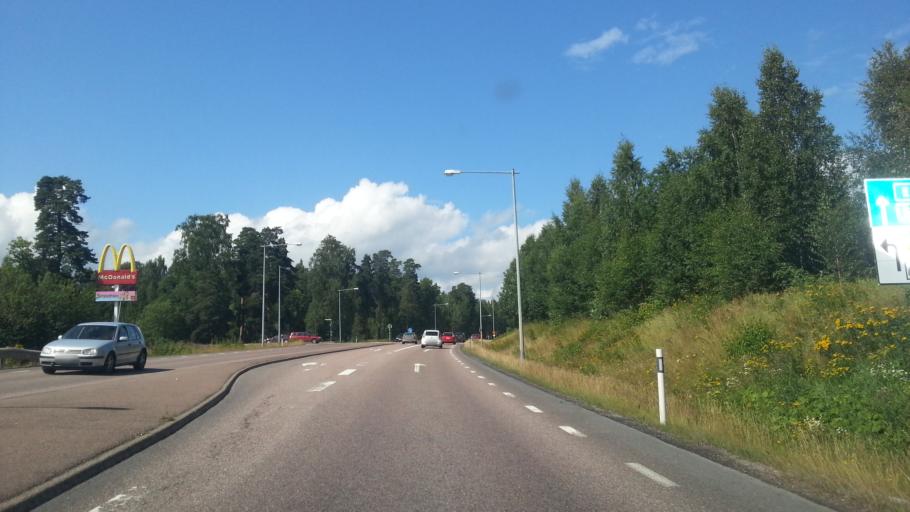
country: SE
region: Dalarna
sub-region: Faluns Kommun
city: Falun
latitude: 60.6090
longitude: 15.6567
